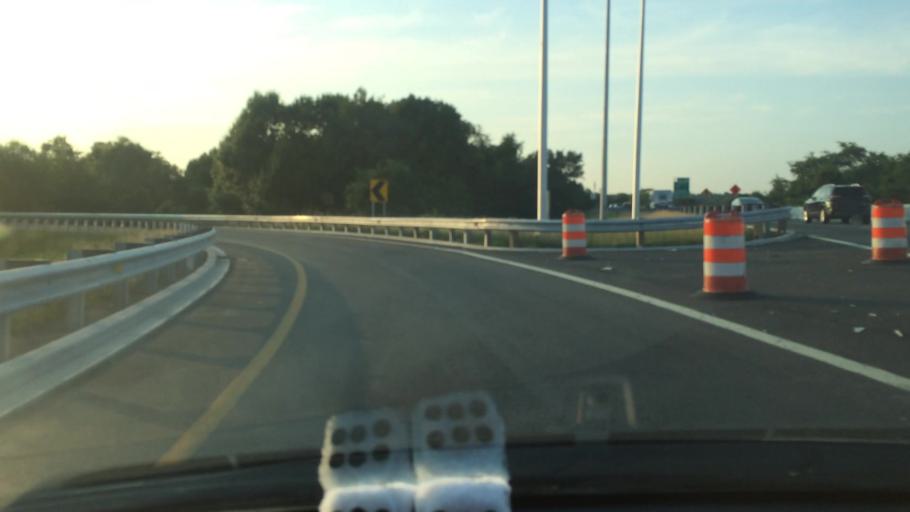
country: US
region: Delaware
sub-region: New Castle County
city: Newport
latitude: 39.7013
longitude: -75.6019
